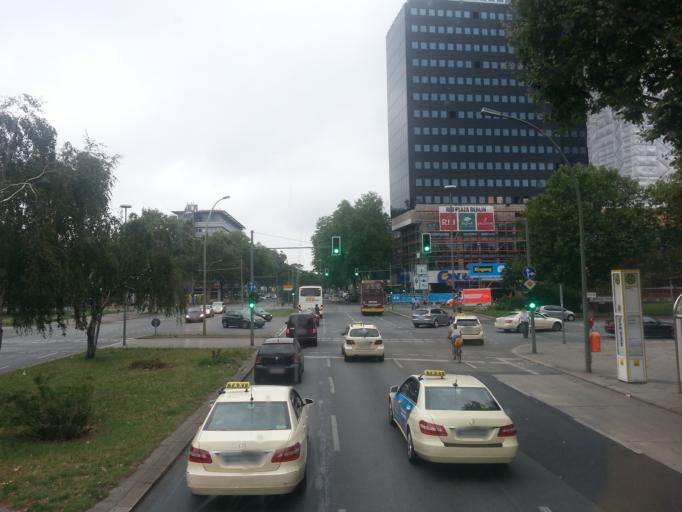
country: DE
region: Berlin
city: Berlin Schoeneberg
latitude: 52.5012
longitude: 13.3456
